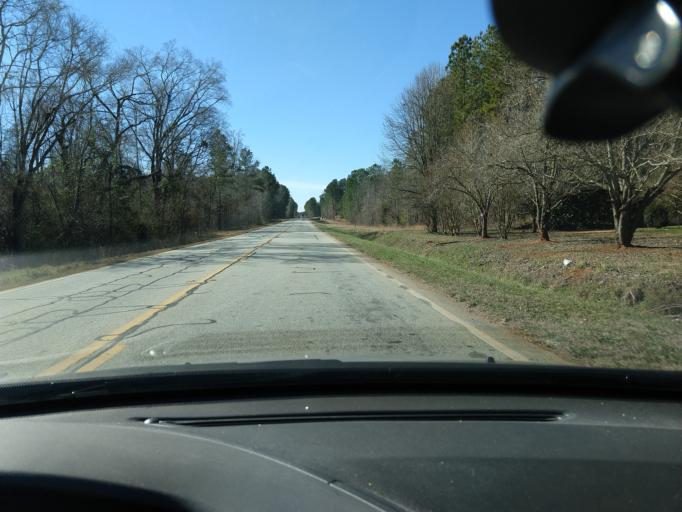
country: US
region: Georgia
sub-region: Jasper County
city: Monticello
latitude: 33.2325
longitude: -83.7338
